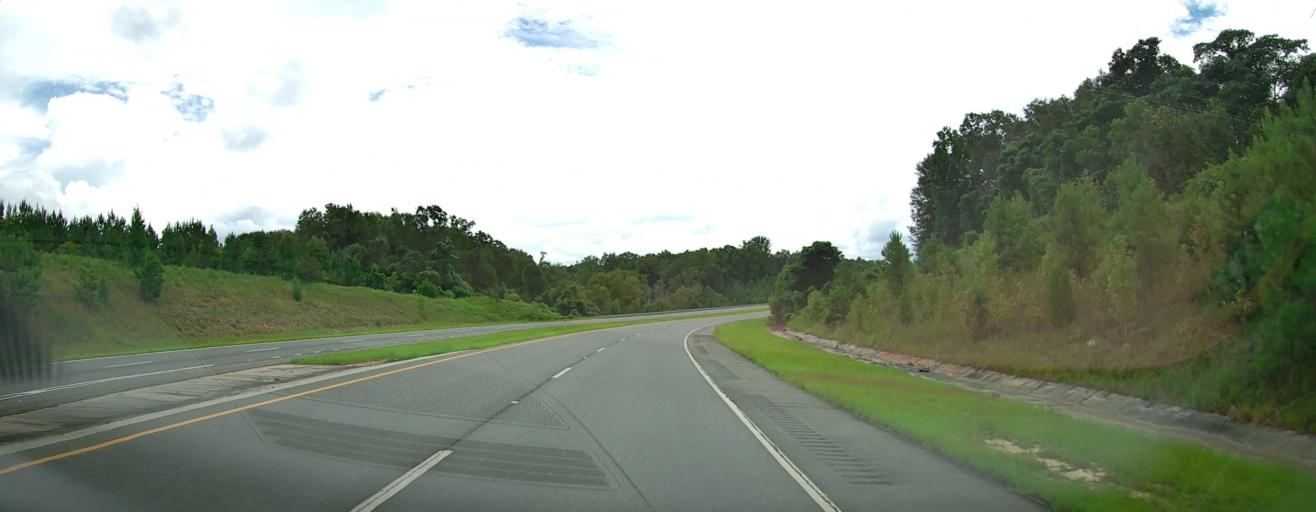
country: US
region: Georgia
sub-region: Schley County
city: Ellaville
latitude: 32.2508
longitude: -84.2971
